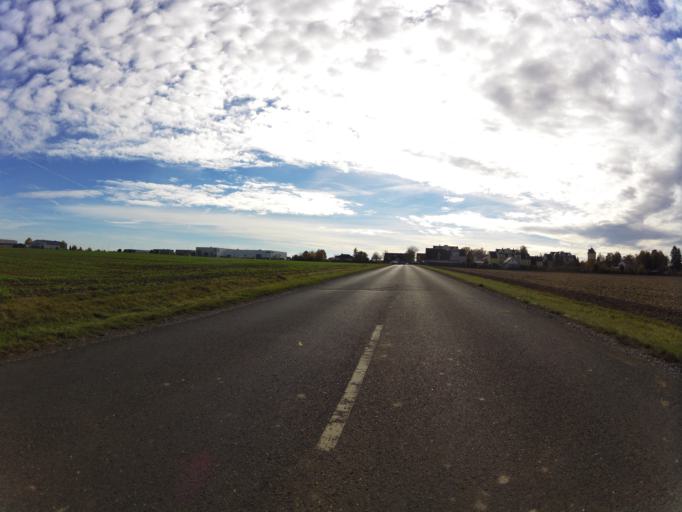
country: DE
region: Bavaria
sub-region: Regierungsbezirk Unterfranken
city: Giebelstadt
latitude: 49.6562
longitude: 9.9521
